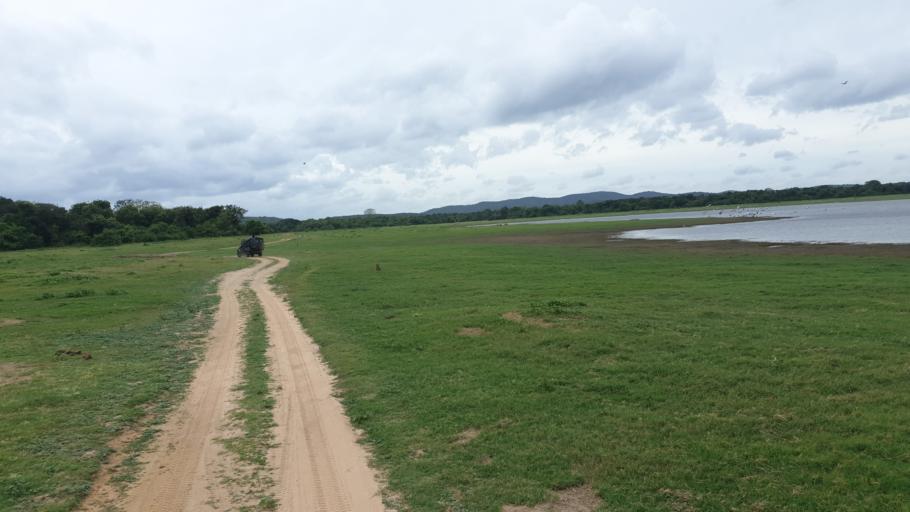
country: LK
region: North Central
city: Polonnaruwa
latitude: 8.1323
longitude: 80.9119
